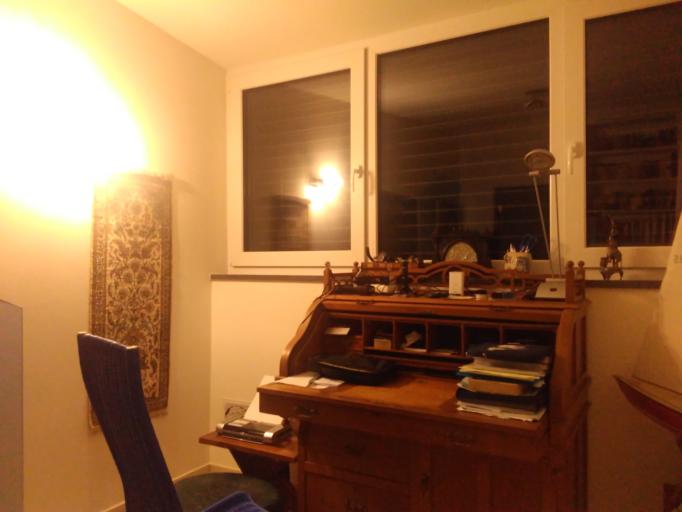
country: DE
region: Baden-Wuerttemberg
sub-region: Tuebingen Region
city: Wangen im Allgau
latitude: 47.6881
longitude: 9.8204
